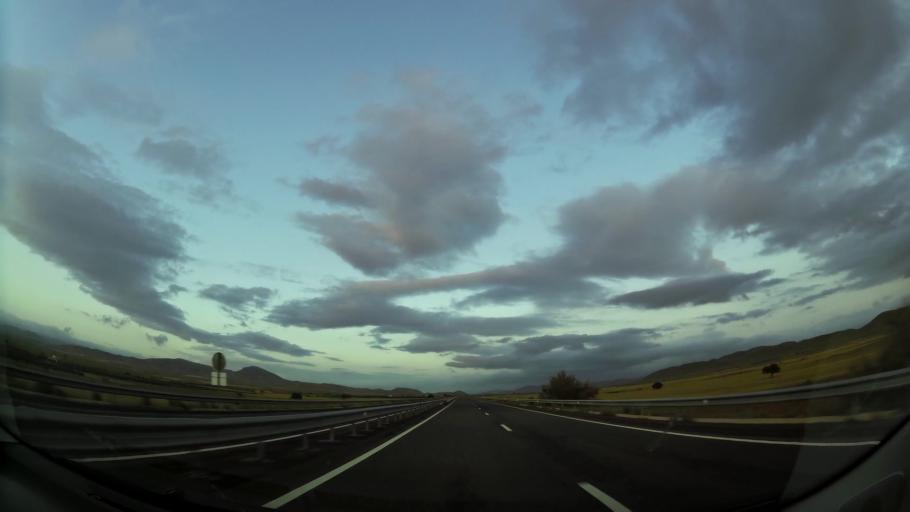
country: MA
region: Oriental
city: El Aioun
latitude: 34.5977
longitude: -2.7253
